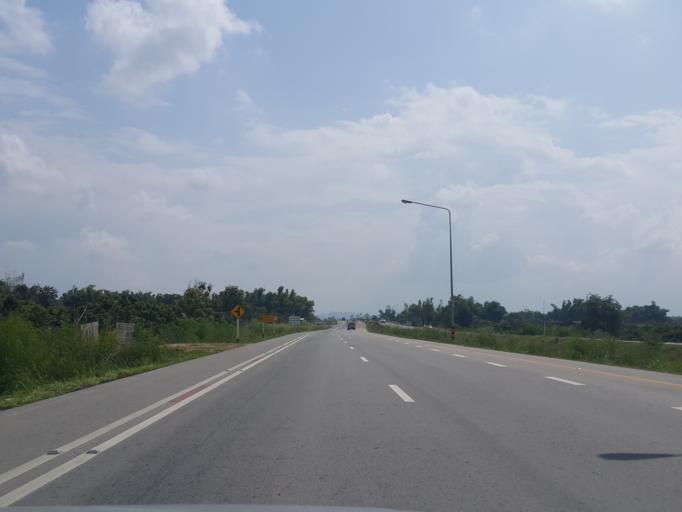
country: TH
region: Lamphun
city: Pa Sang
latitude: 18.5410
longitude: 98.8543
